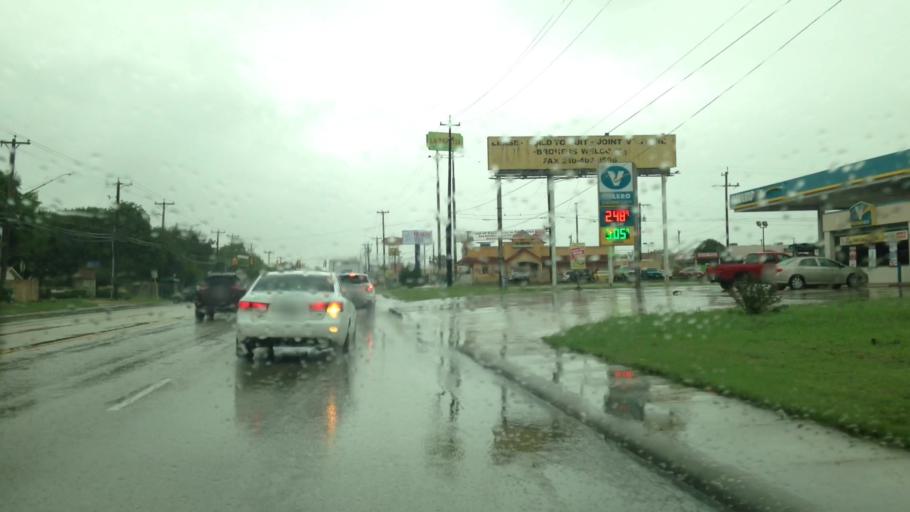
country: US
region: Texas
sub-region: Bexar County
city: Windcrest
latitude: 29.5190
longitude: -98.4109
